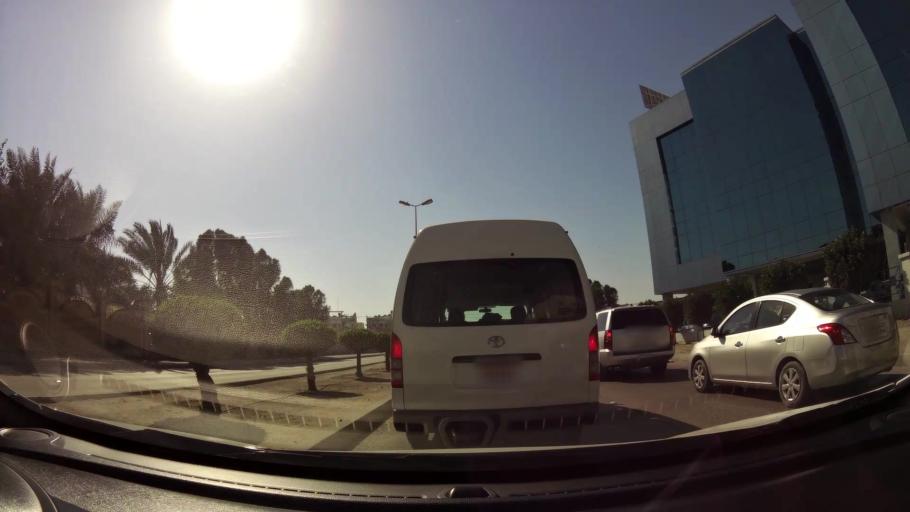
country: BH
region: Manama
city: Manama
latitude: 26.2127
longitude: 50.5709
